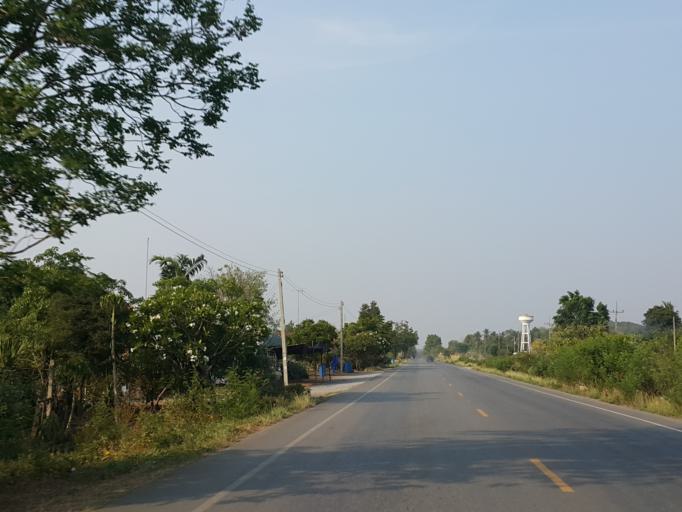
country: TH
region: Chai Nat
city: Sankhaburi
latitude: 15.0010
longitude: 100.1229
